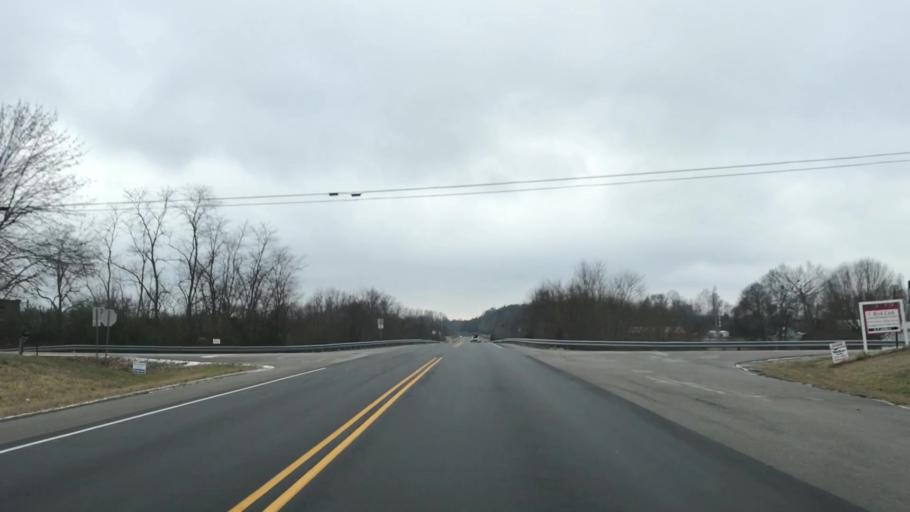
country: US
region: Kentucky
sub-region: Metcalfe County
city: Edmonton
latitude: 36.9571
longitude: -85.4392
